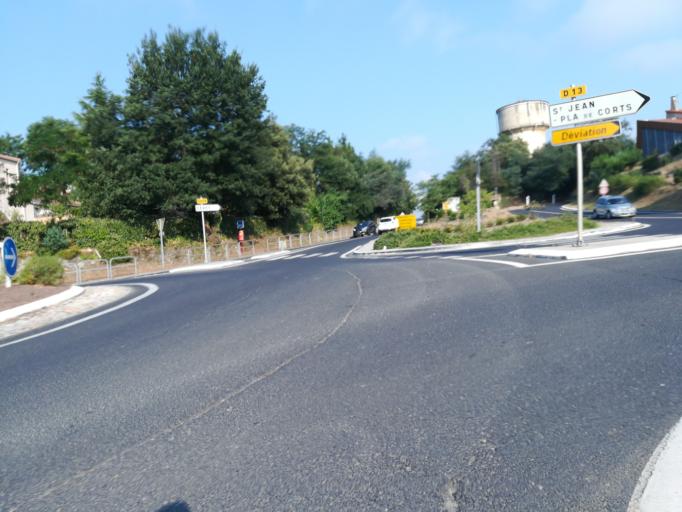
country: FR
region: Languedoc-Roussillon
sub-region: Departement des Pyrenees-Orientales
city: Maureillas-las-Illas
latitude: 42.4903
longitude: 2.8030
